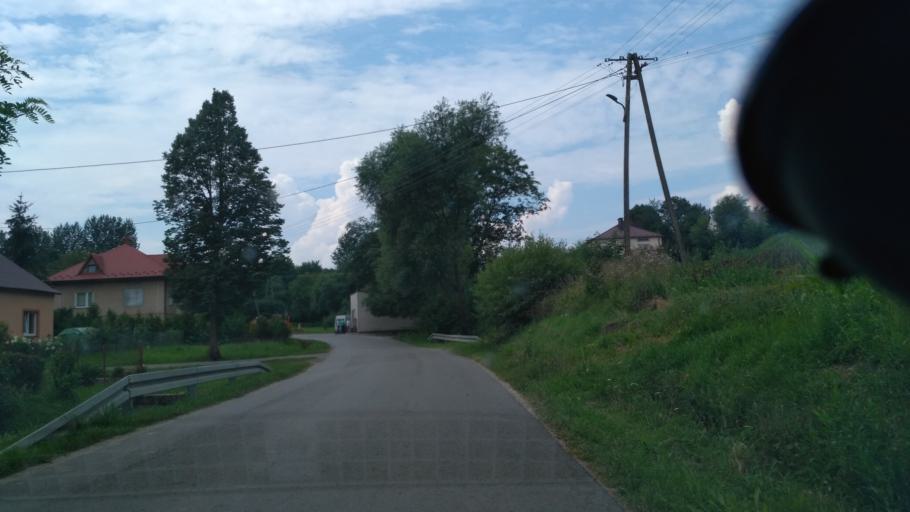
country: PL
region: Subcarpathian Voivodeship
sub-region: Powiat przeworski
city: Lopuszka Wielka
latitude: 49.9184
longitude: 22.4152
